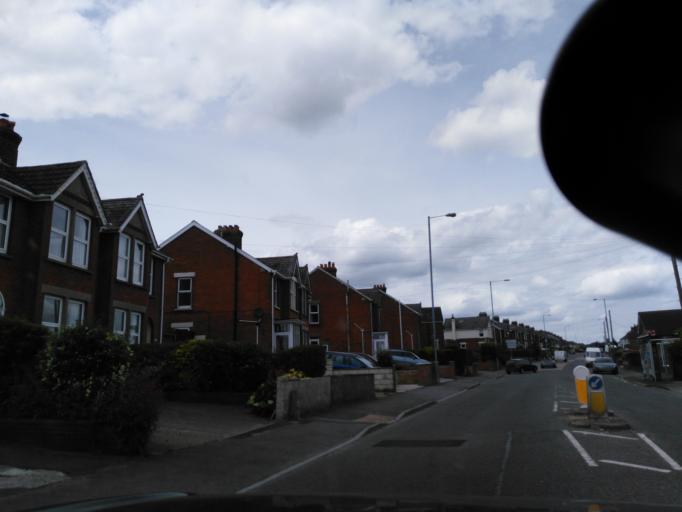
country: GB
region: England
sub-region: Wiltshire
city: Salisbury
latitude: 51.0818
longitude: -1.8186
